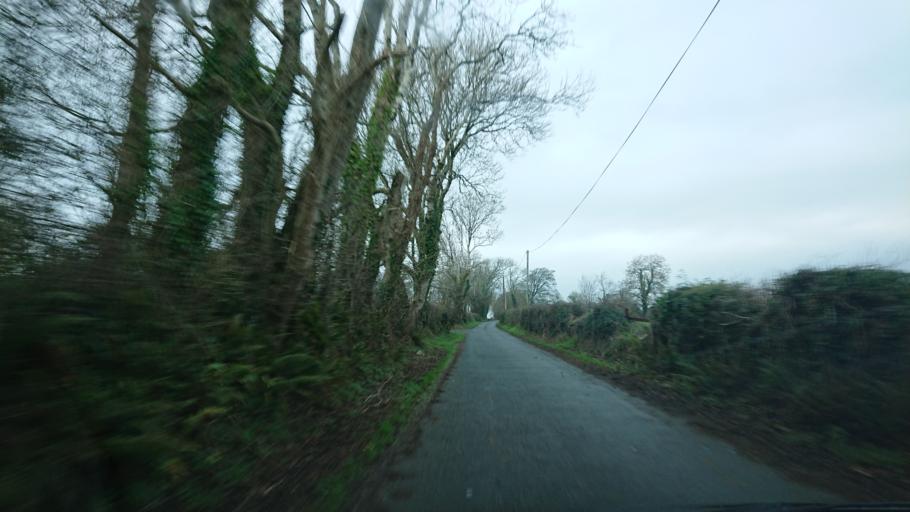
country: IE
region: Munster
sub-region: Waterford
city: Dunmore East
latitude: 52.2021
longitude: -7.0121
